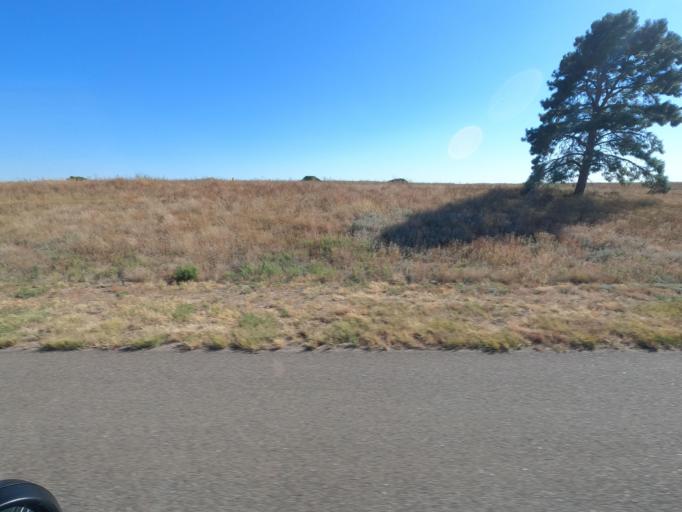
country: US
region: Nebraska
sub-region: Cheyenne County
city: Sidney
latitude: 40.8321
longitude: -102.7733
